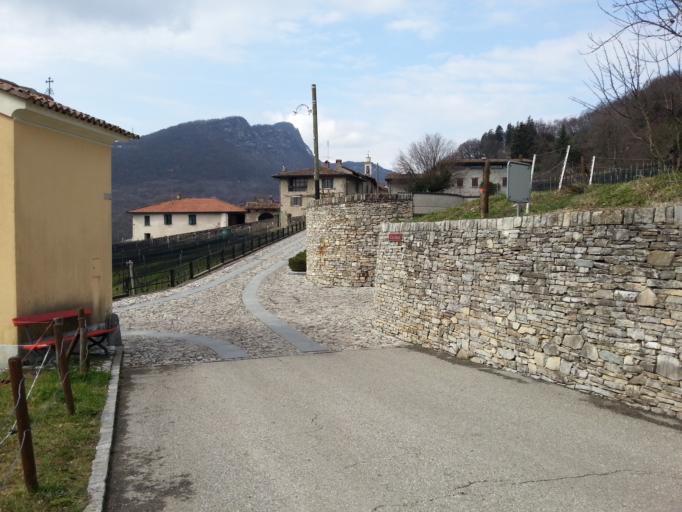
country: CH
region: Ticino
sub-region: Mendrisio District
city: Riva San Vitale
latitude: 45.8899
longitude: 8.9570
